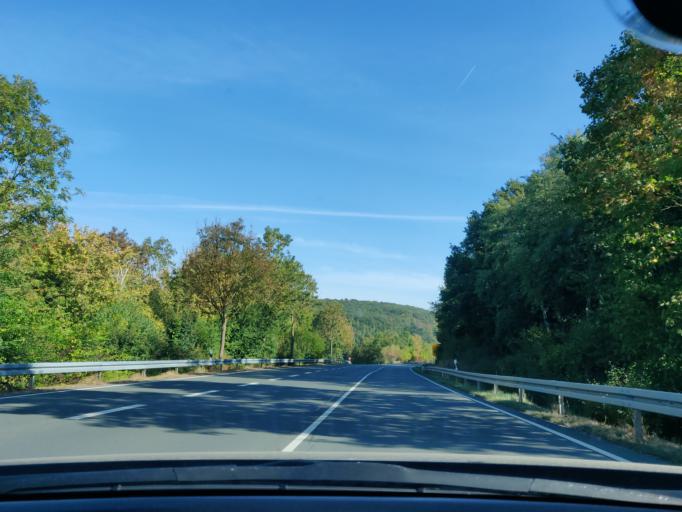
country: DE
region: Hesse
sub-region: Regierungsbezirk Kassel
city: Bad Wildungen
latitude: 51.1218
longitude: 9.1568
